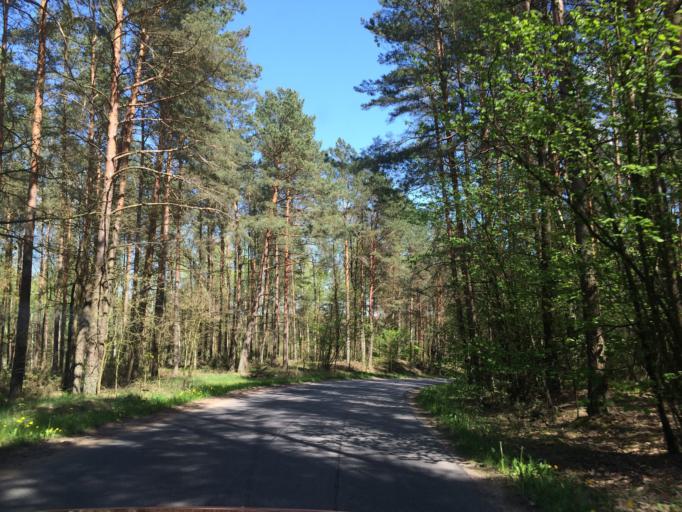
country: PL
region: Warmian-Masurian Voivodeship
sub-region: Powiat ilawski
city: Lubawa
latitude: 53.3884
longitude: 19.7267
